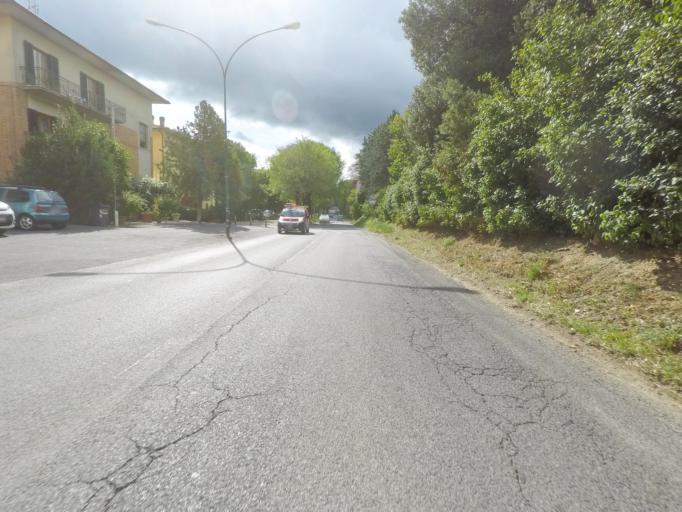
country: IT
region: Tuscany
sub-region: Provincia di Siena
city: Montepulciano
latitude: 43.1048
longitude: 11.7859
